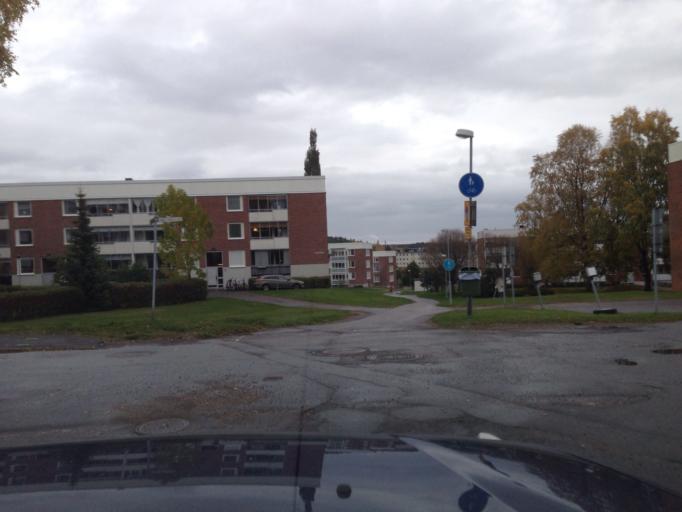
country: SE
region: Vaesternorrland
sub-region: Sundsvalls Kommun
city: Sundsvall
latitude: 62.3993
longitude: 17.3307
